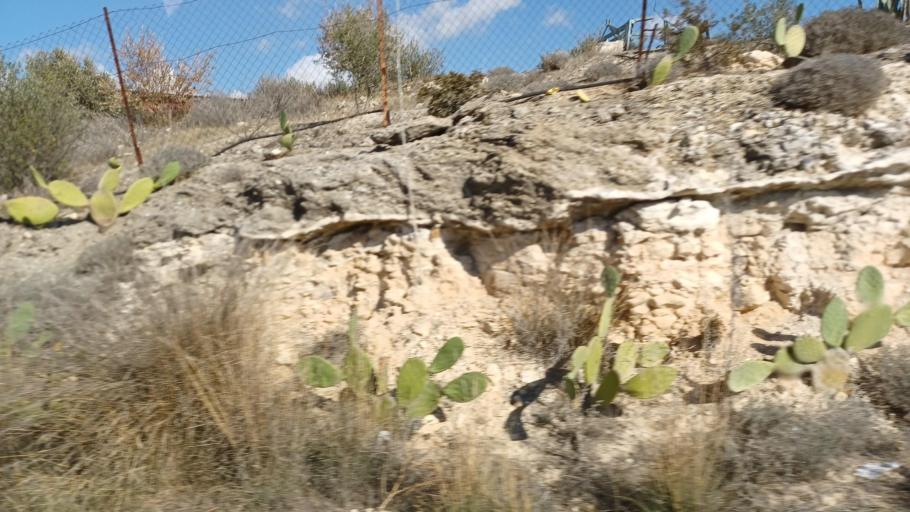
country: CY
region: Larnaka
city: Voroklini
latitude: 35.0072
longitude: 33.6475
